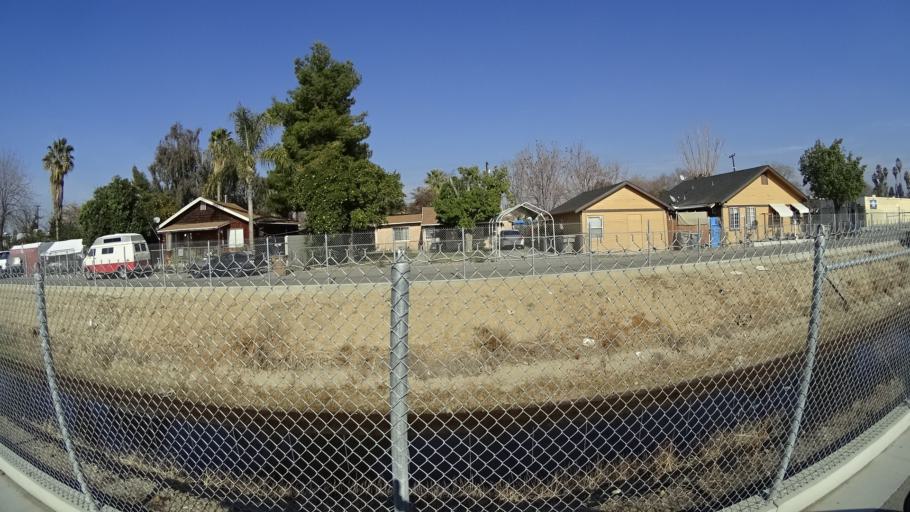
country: US
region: California
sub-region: Kern County
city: Bakersfield
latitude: 35.3815
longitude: -118.9985
